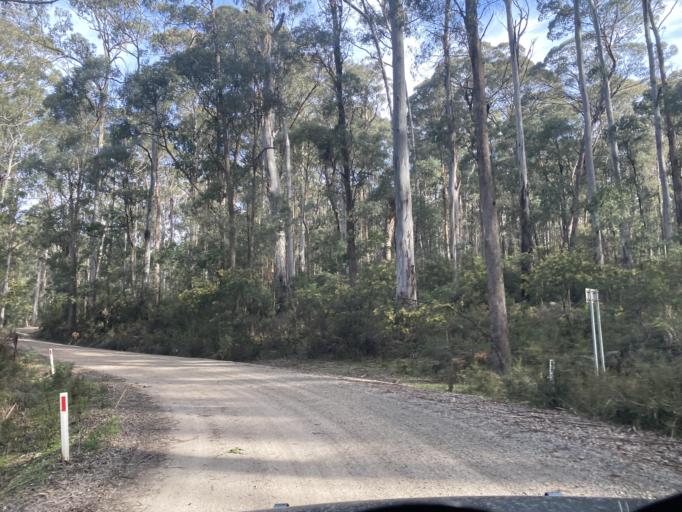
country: AU
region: Victoria
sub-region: Mansfield
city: Mansfield
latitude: -36.8555
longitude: 146.1918
